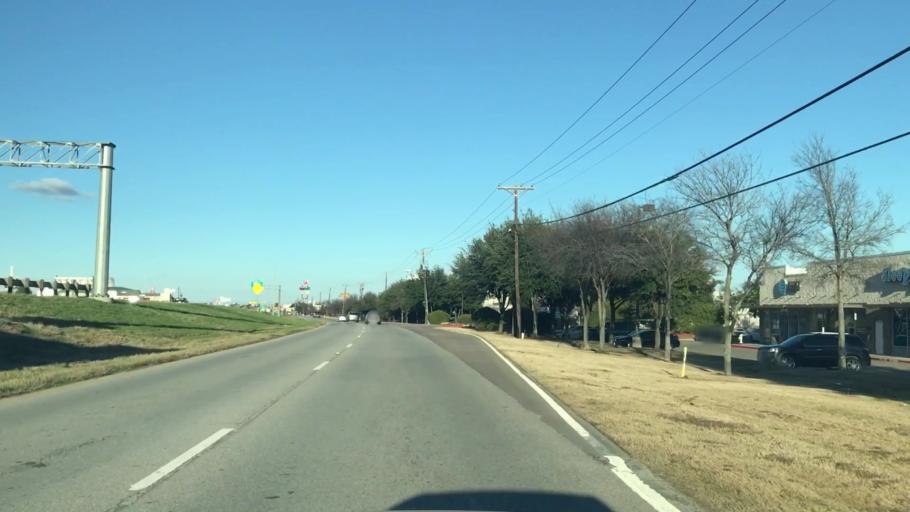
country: US
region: Texas
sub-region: Rockwall County
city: Rockwall
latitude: 32.9019
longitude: -96.4560
